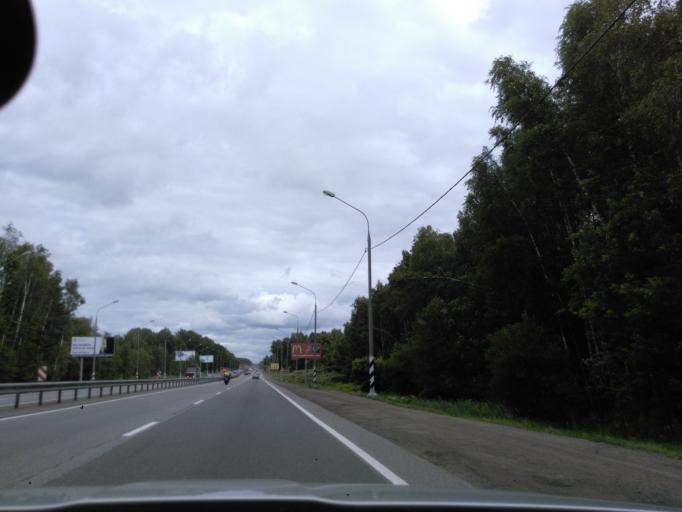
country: RU
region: Moskovskaya
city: Chashnikovo
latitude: 56.0214
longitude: 37.1894
